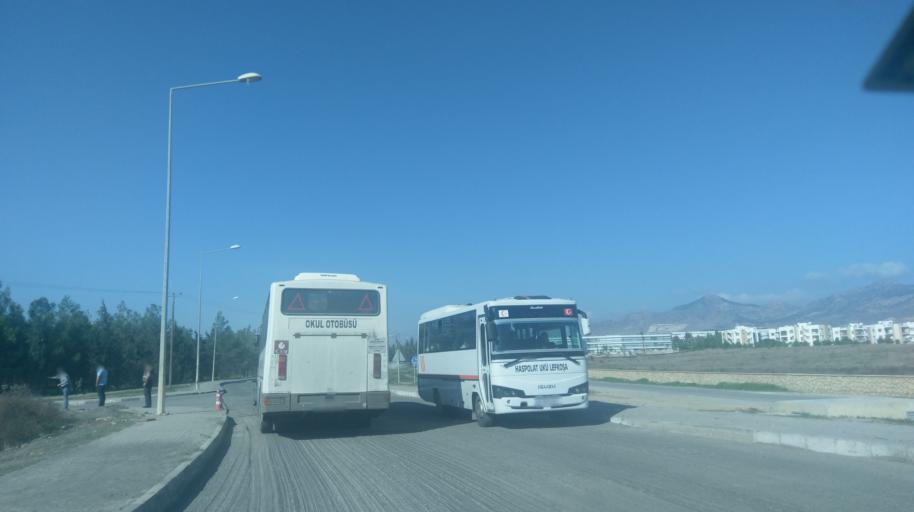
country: CY
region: Lefkosia
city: Nicosia
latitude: 35.2182
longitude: 33.4212
